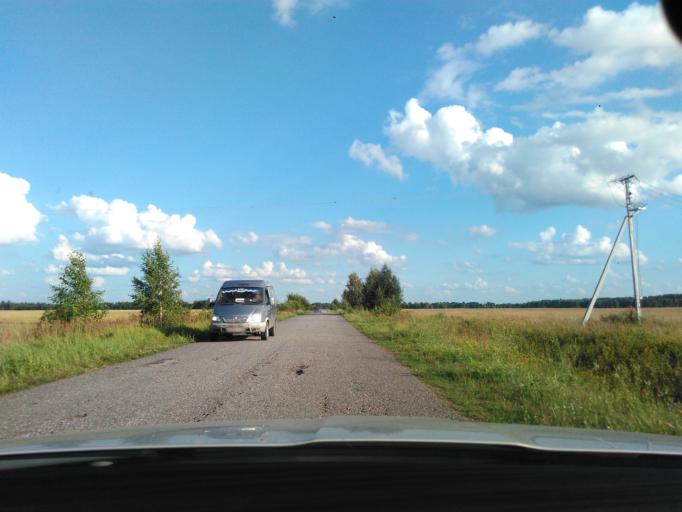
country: RU
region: Tverskaya
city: Zavidovo
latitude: 56.6026
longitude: 36.5959
